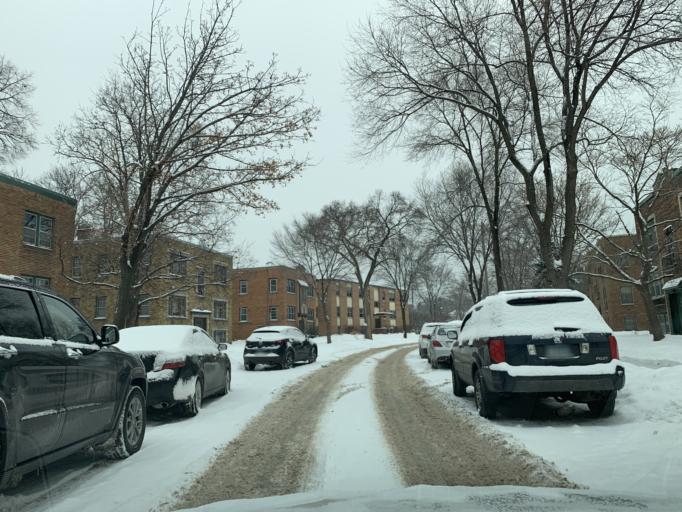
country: US
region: Minnesota
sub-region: Hennepin County
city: Saint Louis Park
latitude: 44.9525
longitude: -93.3188
